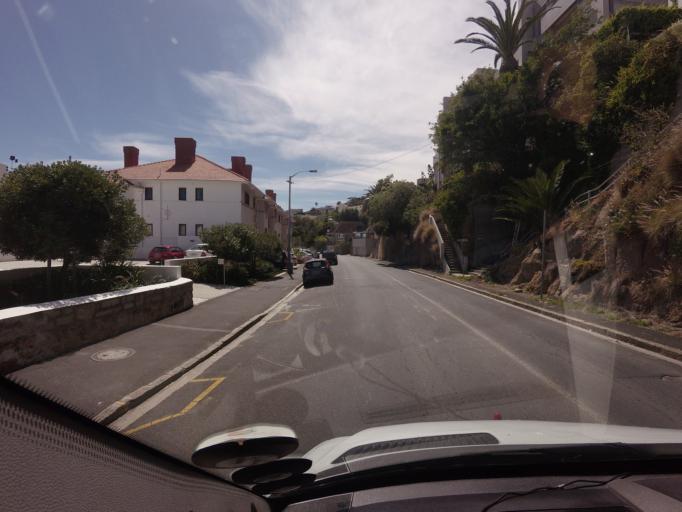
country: ZA
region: Western Cape
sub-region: City of Cape Town
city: Cape Town
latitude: -33.9281
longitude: 18.3769
